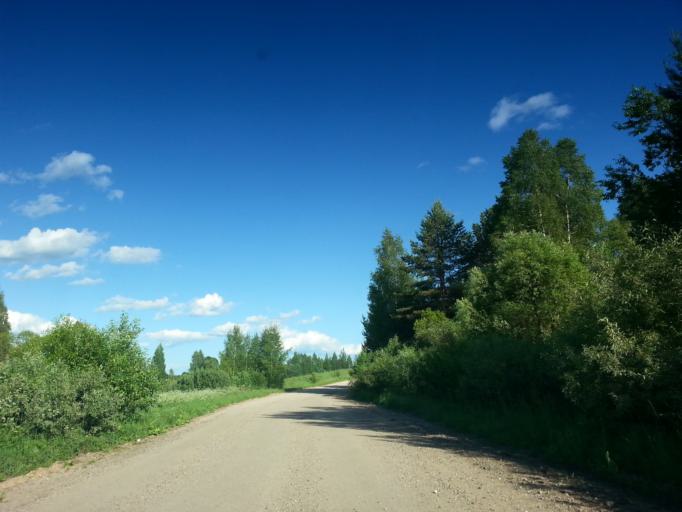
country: BY
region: Minsk
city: Narach
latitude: 54.9775
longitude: 26.6205
